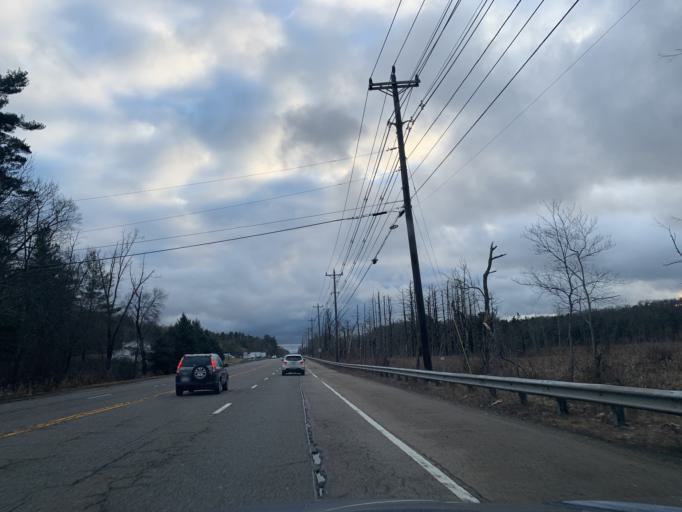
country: US
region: Massachusetts
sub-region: Norfolk County
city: Wrentham
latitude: 42.0615
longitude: -71.2956
